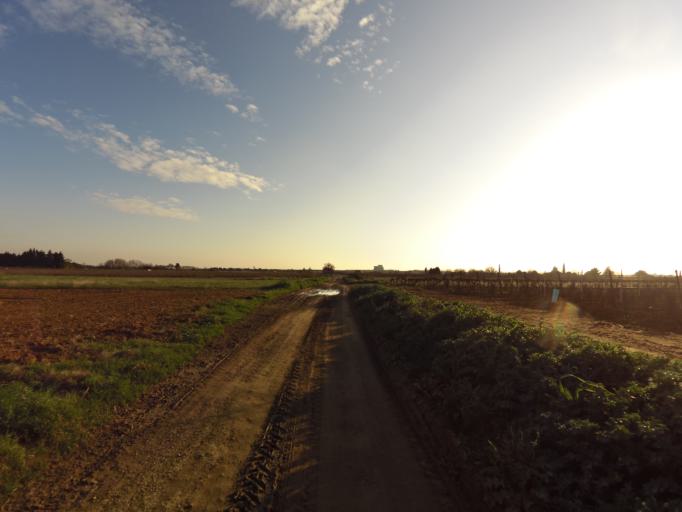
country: FR
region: Languedoc-Roussillon
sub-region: Departement du Gard
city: Gallargues-le-Montueux
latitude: 43.7150
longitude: 4.1887
